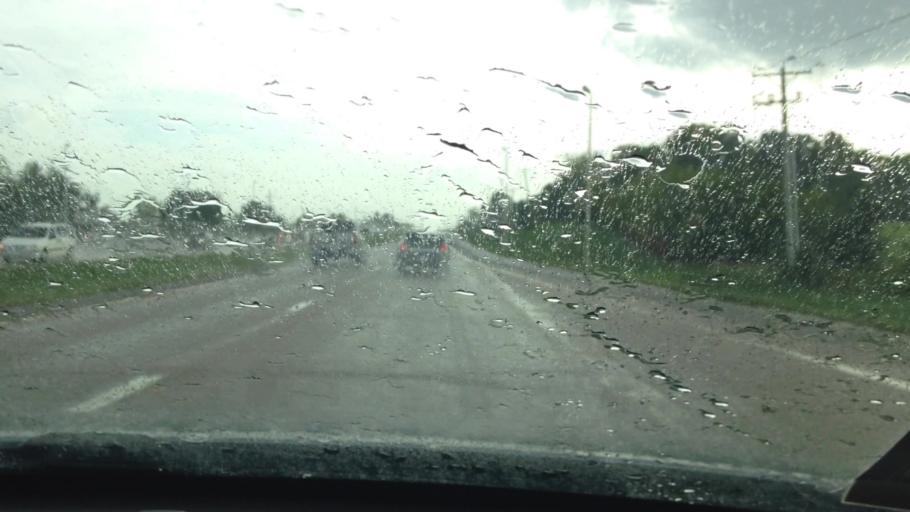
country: US
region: Kansas
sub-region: Leavenworth County
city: Basehor
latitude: 39.1866
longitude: -94.9006
